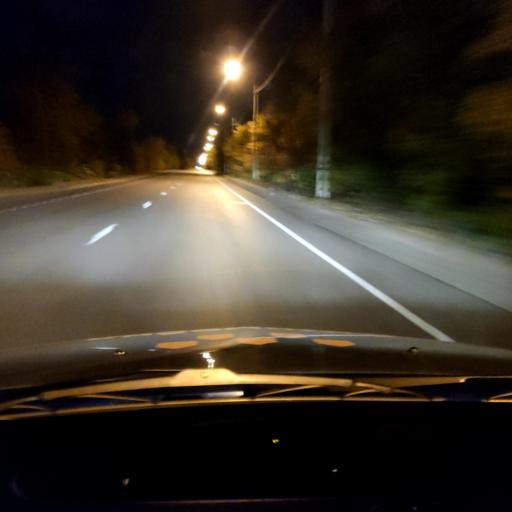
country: RU
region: Voronezj
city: Shilovo
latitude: 51.5781
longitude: 39.1520
